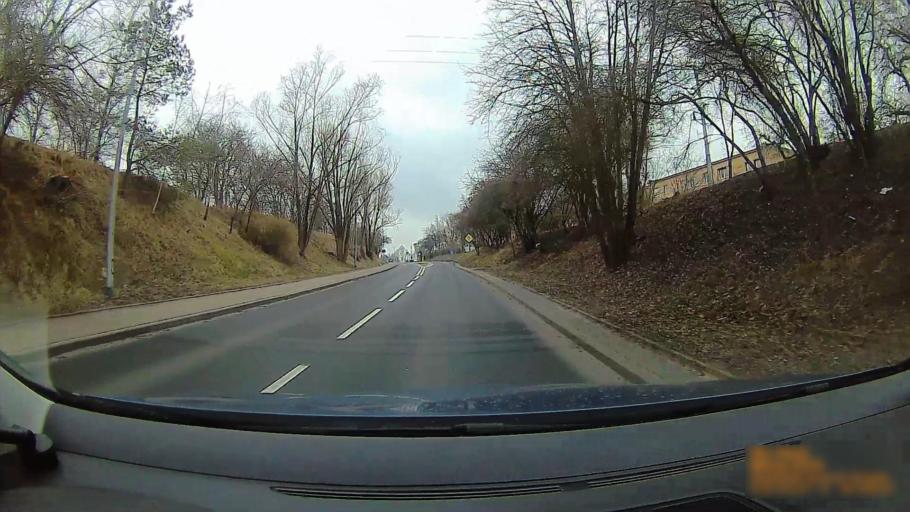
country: PL
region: Greater Poland Voivodeship
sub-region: Konin
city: Konin
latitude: 52.2005
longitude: 18.2613
